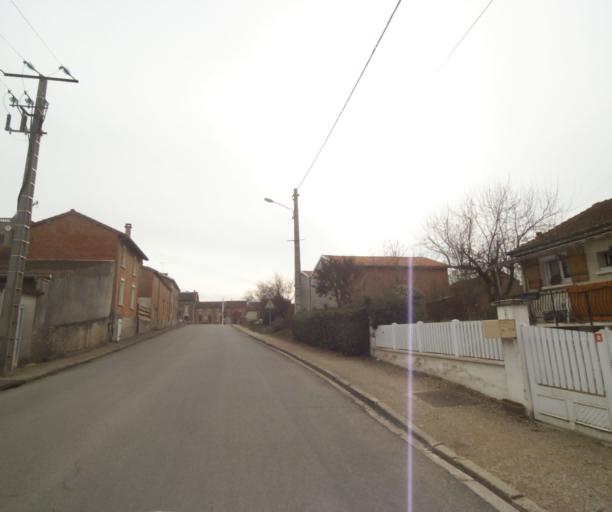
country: FR
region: Champagne-Ardenne
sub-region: Departement de la Marne
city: Pargny-sur-Saulx
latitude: 48.7502
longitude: 4.8494
